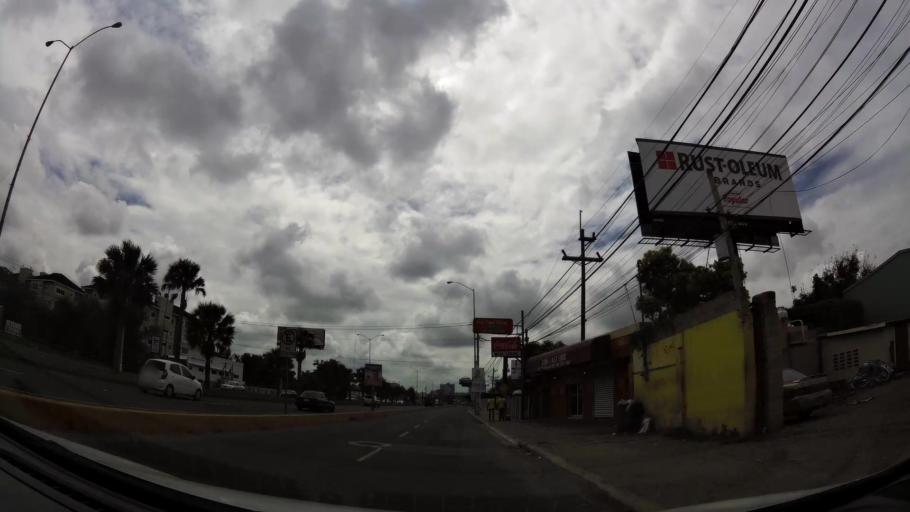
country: DO
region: Santiago
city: Santiago de los Caballeros
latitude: 19.4462
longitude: -70.6738
